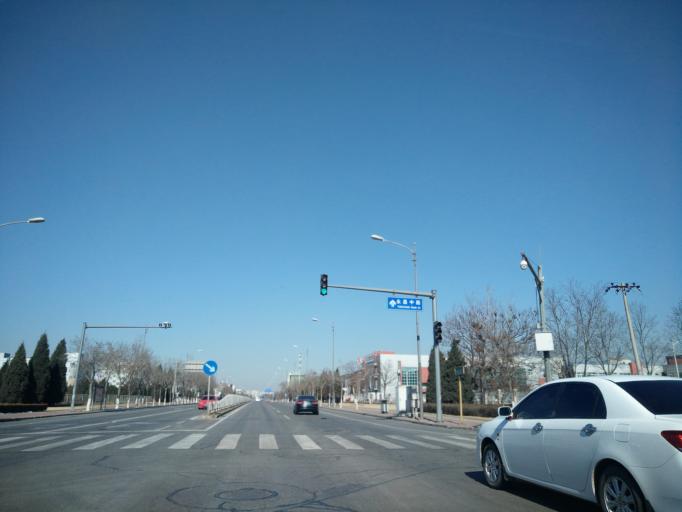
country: CN
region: Beijing
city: Jiugong
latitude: 39.7889
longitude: 116.5159
